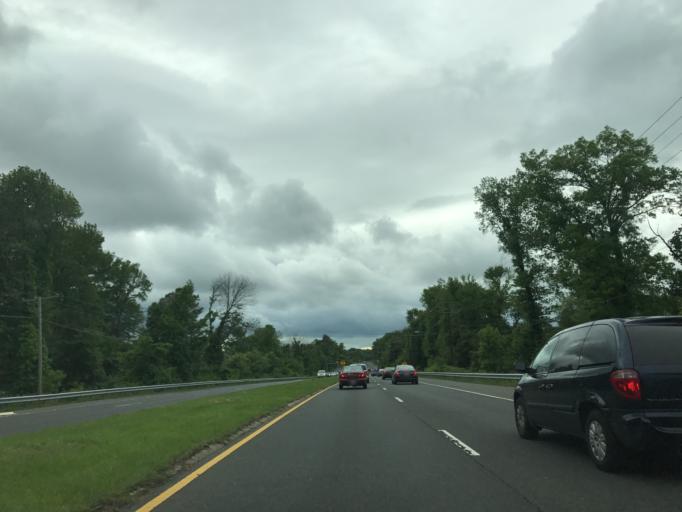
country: US
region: Maryland
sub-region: Prince George's County
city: Chillum
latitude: 38.9680
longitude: -76.9691
